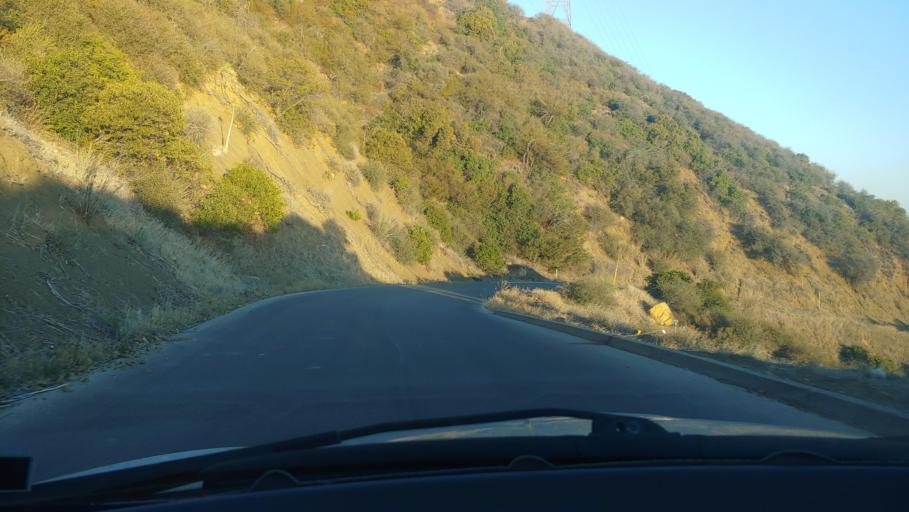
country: US
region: California
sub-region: Santa Barbara County
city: Mission Canyon
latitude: 34.4725
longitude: -119.6792
